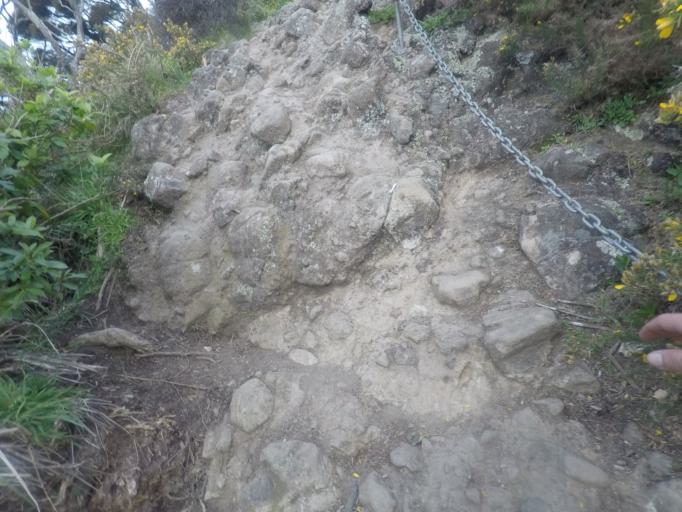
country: NZ
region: Auckland
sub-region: Auckland
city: Muriwai Beach
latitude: -36.9765
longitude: 174.4729
